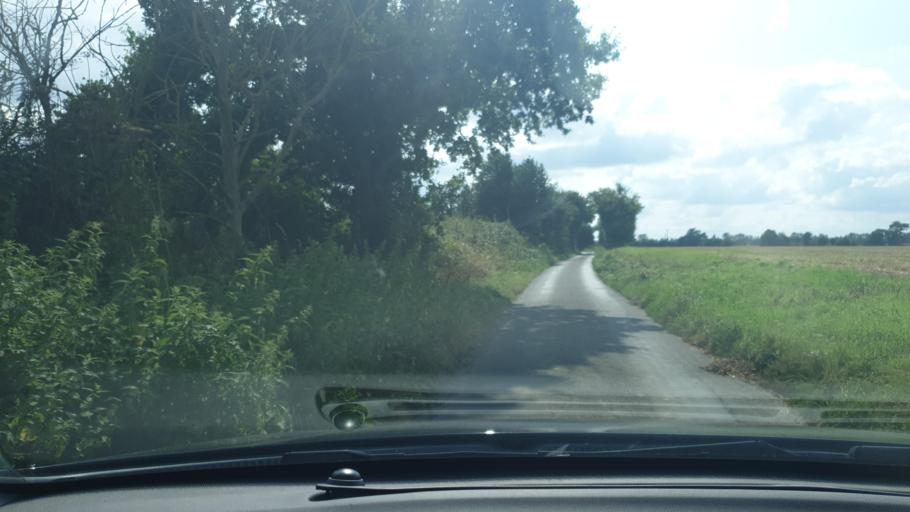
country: GB
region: England
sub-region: Essex
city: Manningtree
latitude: 51.9303
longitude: 1.0330
